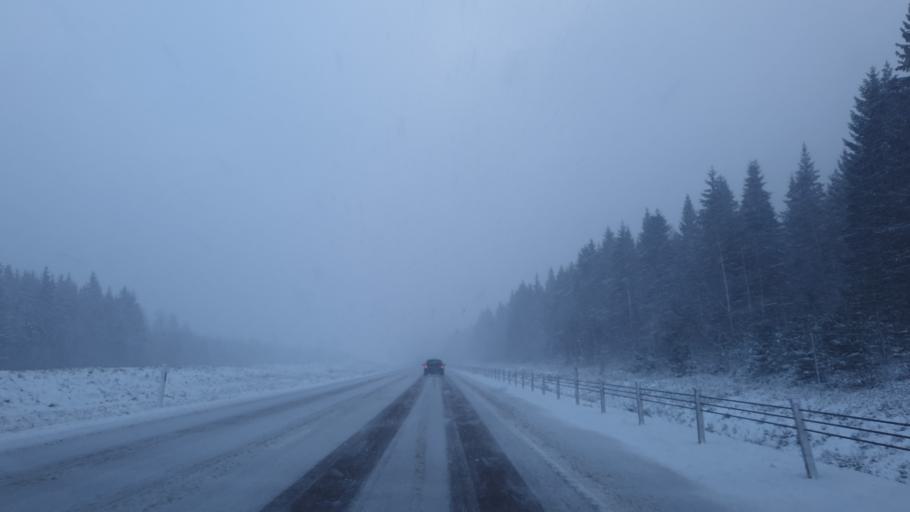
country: SE
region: Uppsala
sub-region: Tierps Kommun
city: Tierp
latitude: 60.4170
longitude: 17.4493
